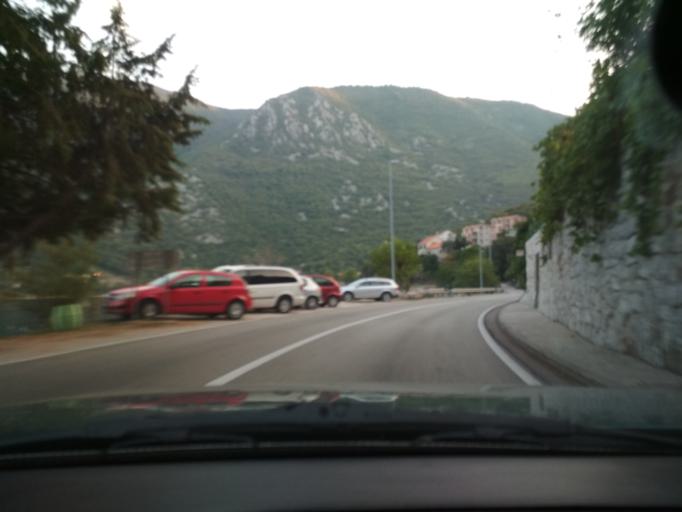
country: ME
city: Lipci
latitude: 42.4936
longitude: 18.6518
